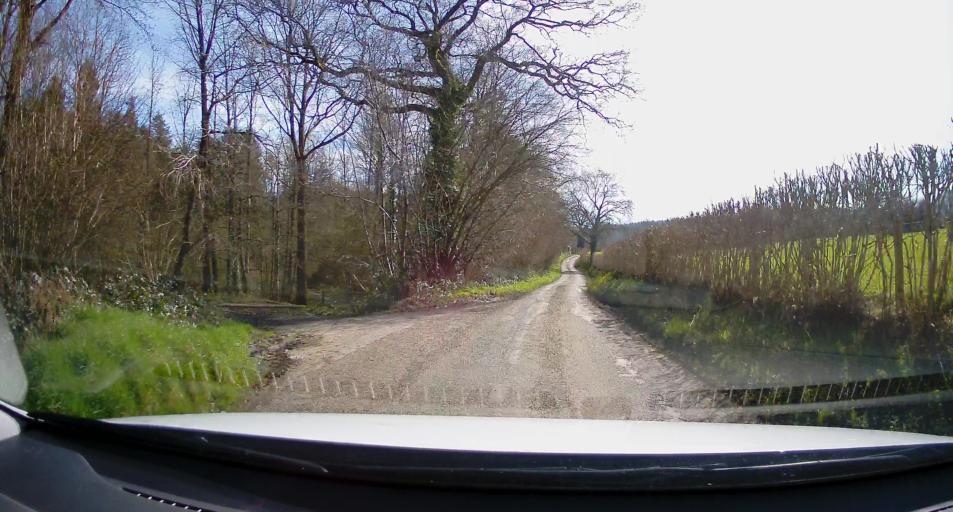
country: GB
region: Wales
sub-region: County of Ceredigion
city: Lledrod
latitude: 52.3357
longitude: -3.9570
